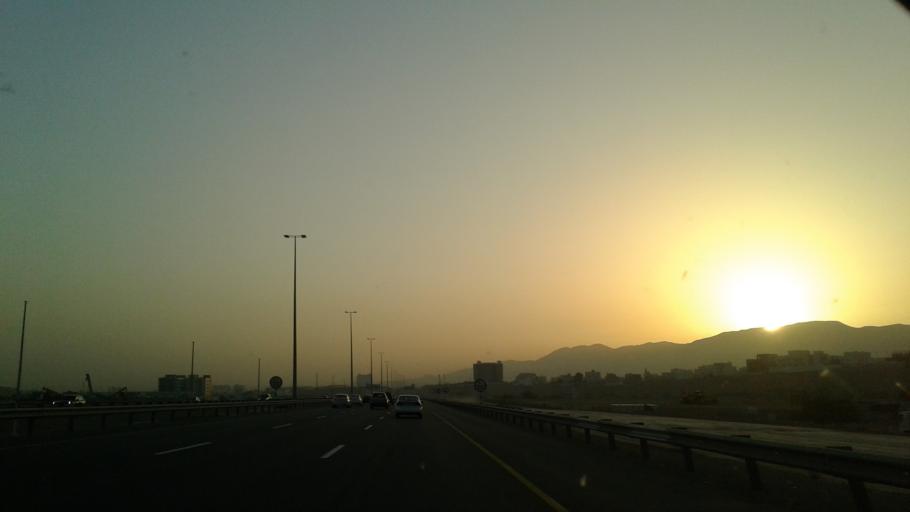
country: OM
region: Muhafazat Masqat
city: Bawshar
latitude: 23.5637
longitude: 58.3517
